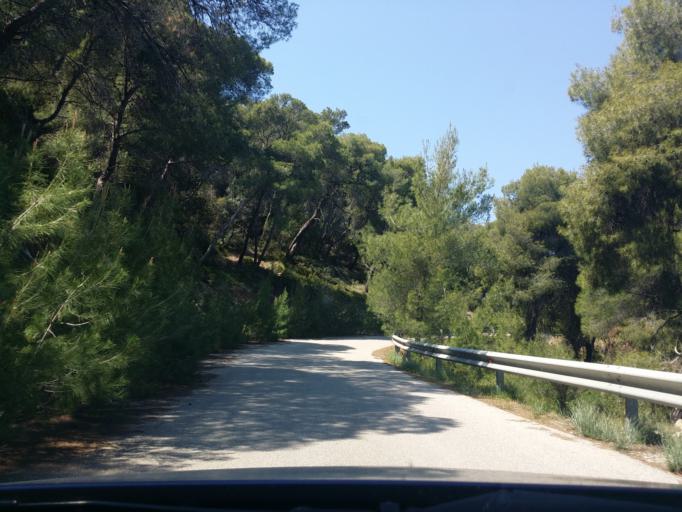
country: GR
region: Attica
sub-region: Nomos Piraios
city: Poros
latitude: 37.5260
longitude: 23.4535
